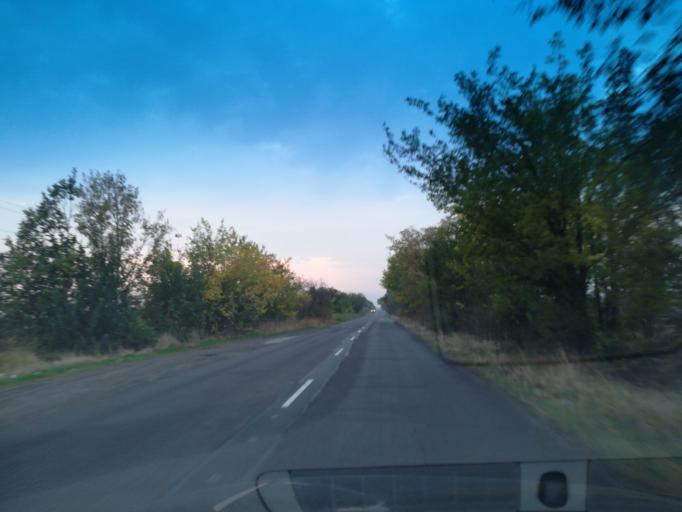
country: BG
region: Stara Zagora
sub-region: Obshtina Chirpan
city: Chirpan
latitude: 42.1900
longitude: 25.2847
